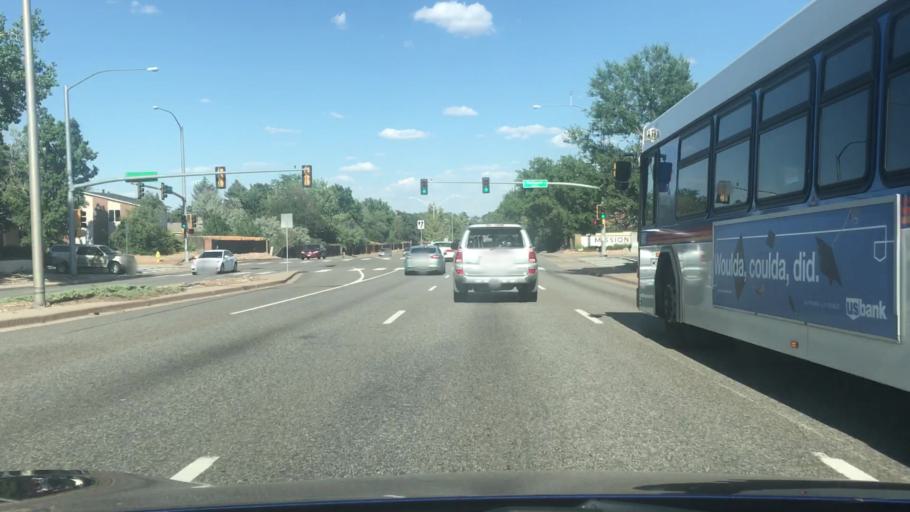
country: US
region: Colorado
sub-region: Arapahoe County
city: Dove Valley
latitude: 39.6530
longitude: -104.8038
